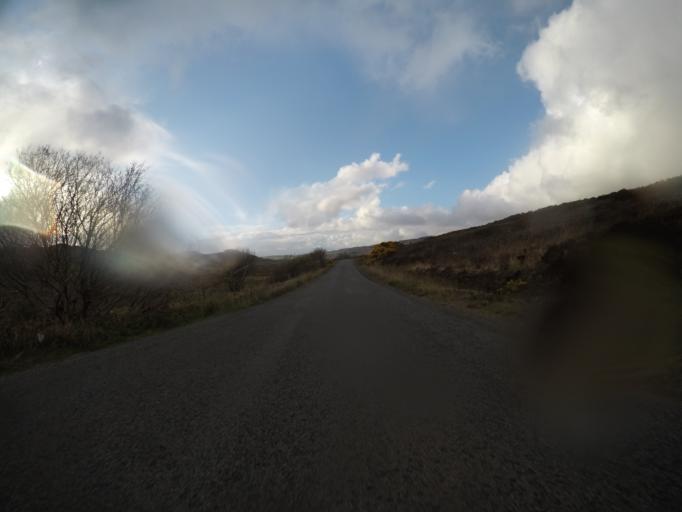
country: GB
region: Scotland
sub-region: Highland
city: Isle of Skye
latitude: 57.4692
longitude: -6.2994
